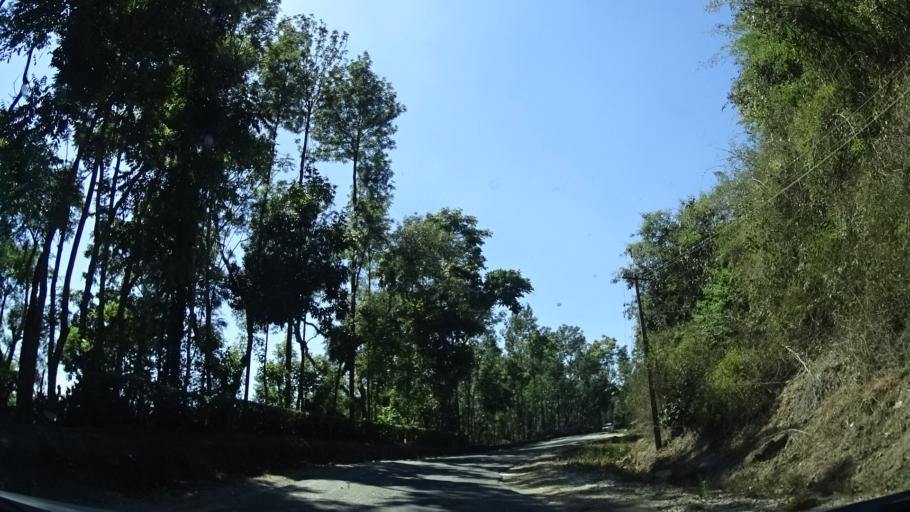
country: IN
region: Karnataka
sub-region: Chikmagalur
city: Mudigere
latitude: 13.1687
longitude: 75.6525
